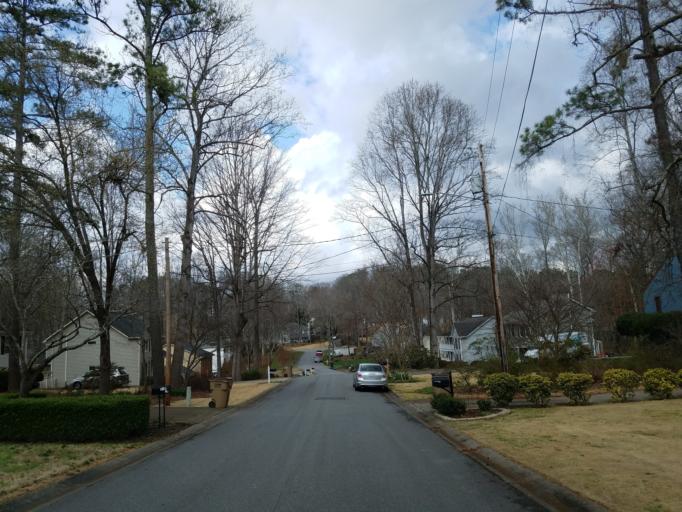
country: US
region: Georgia
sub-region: Cherokee County
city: Woodstock
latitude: 34.0285
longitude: -84.5023
